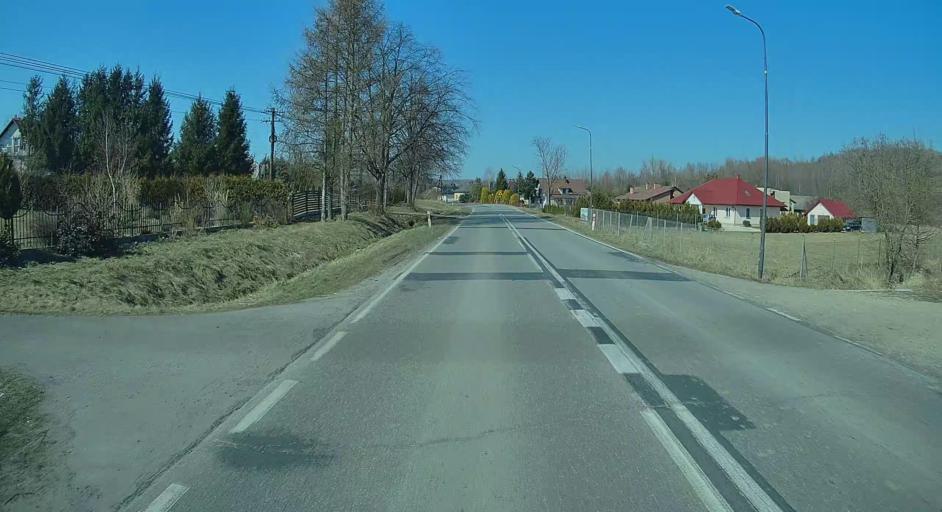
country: PL
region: Subcarpathian Voivodeship
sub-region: Powiat rzeszowski
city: Blazowa
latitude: 49.9360
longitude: 22.1093
